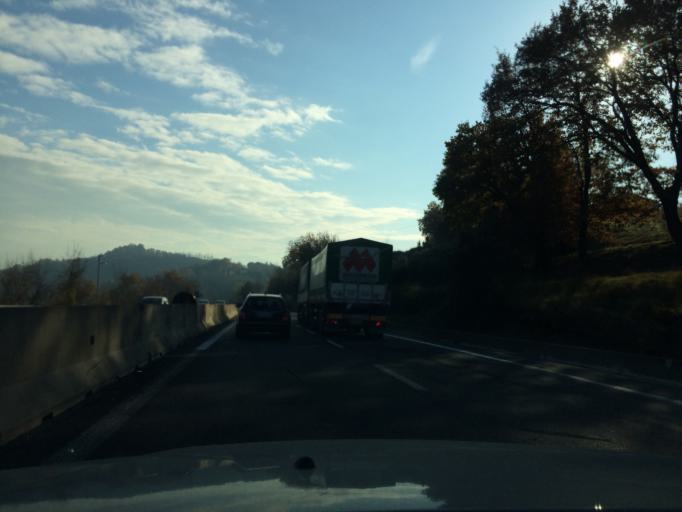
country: IT
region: Umbria
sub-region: Provincia di Terni
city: San Gemini
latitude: 42.6111
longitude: 12.5549
